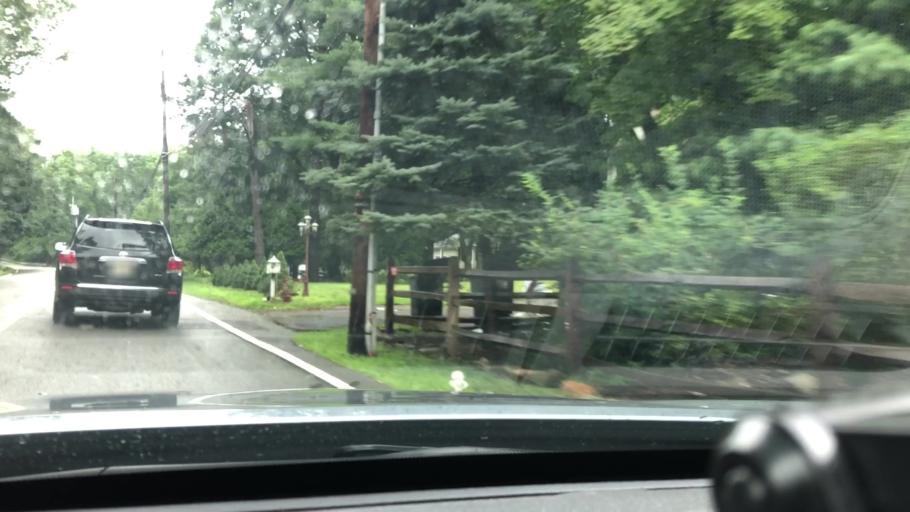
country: US
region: New Jersey
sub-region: Bergen County
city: Saddle River
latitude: 41.0244
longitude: -74.1028
